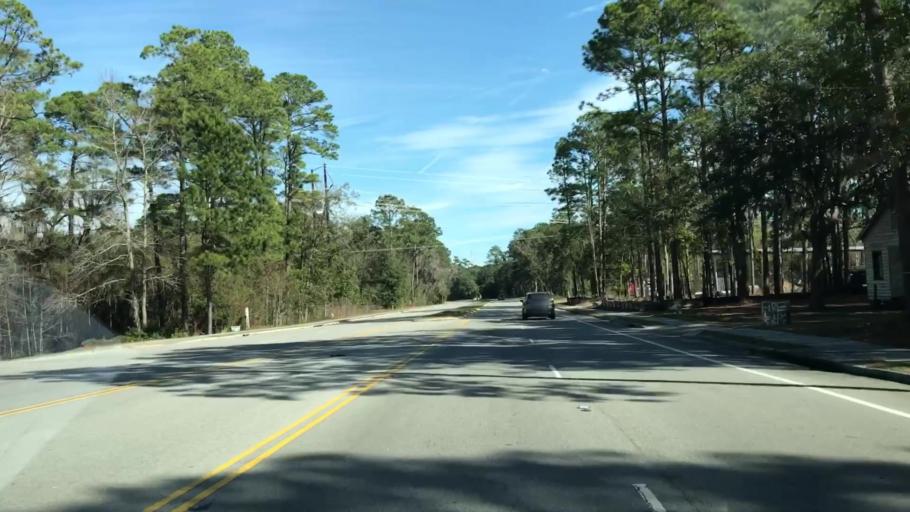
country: US
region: South Carolina
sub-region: Beaufort County
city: Bluffton
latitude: 32.2632
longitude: -80.8690
